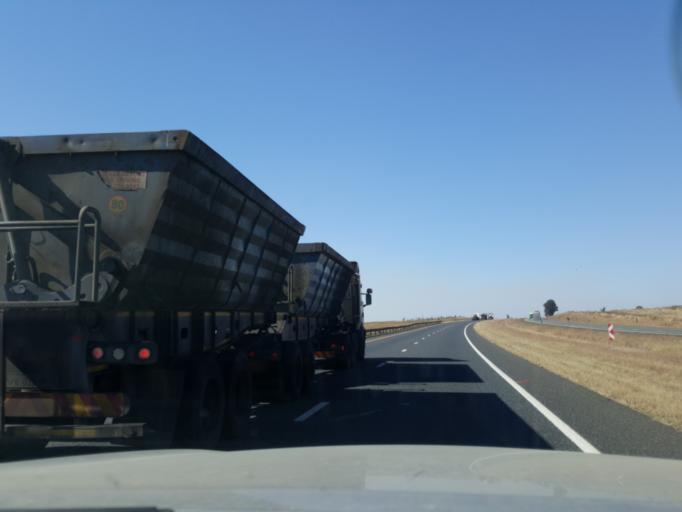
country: ZA
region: Mpumalanga
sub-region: Nkangala District Municipality
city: Delmas
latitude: -26.0186
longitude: 28.9018
